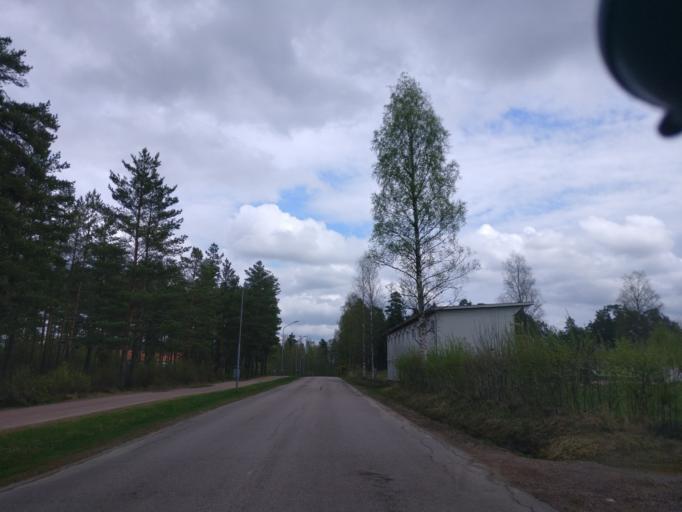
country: SE
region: Vaermland
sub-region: Hagfors Kommun
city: Ekshaerad
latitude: 60.1743
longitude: 13.4870
